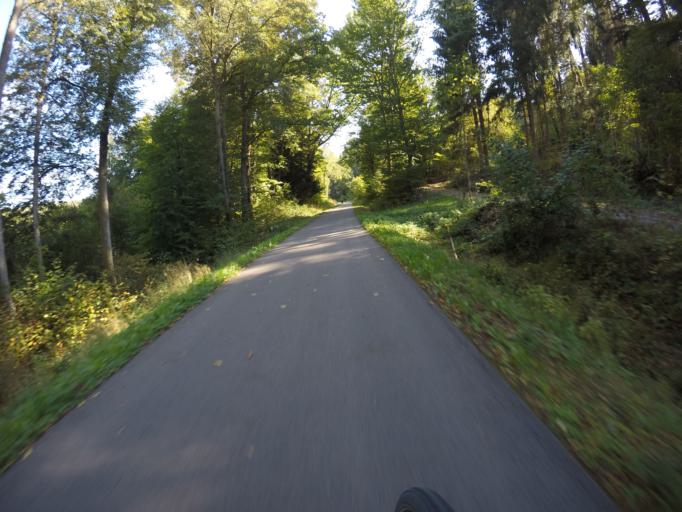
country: DE
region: Baden-Wuerttemberg
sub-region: Regierungsbezirk Stuttgart
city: Waldenbuch
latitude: 48.6630
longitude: 9.1450
